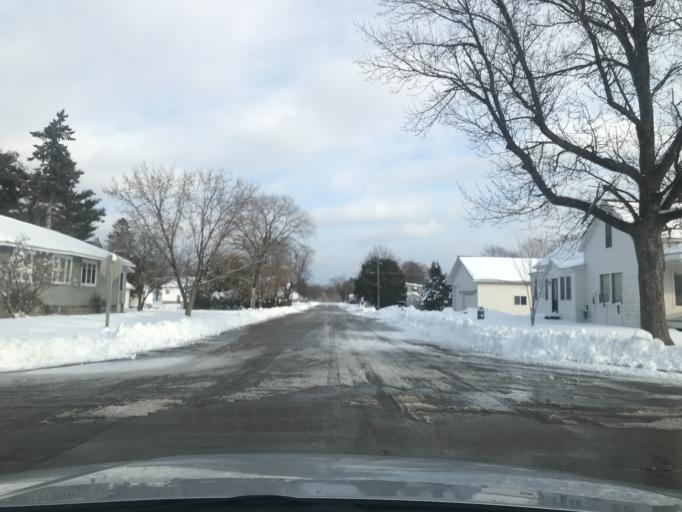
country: US
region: Wisconsin
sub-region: Marinette County
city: Peshtigo
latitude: 45.0485
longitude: -87.7528
